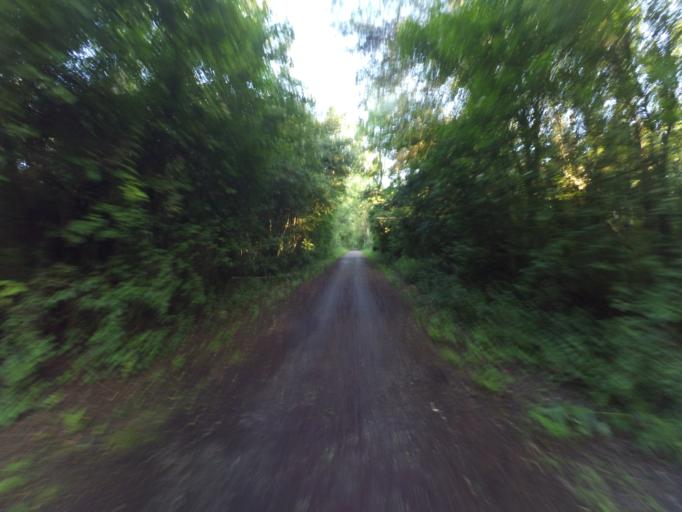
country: DE
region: Bavaria
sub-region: Upper Bavaria
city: Oberschleissheim
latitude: 48.2298
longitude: 11.5687
